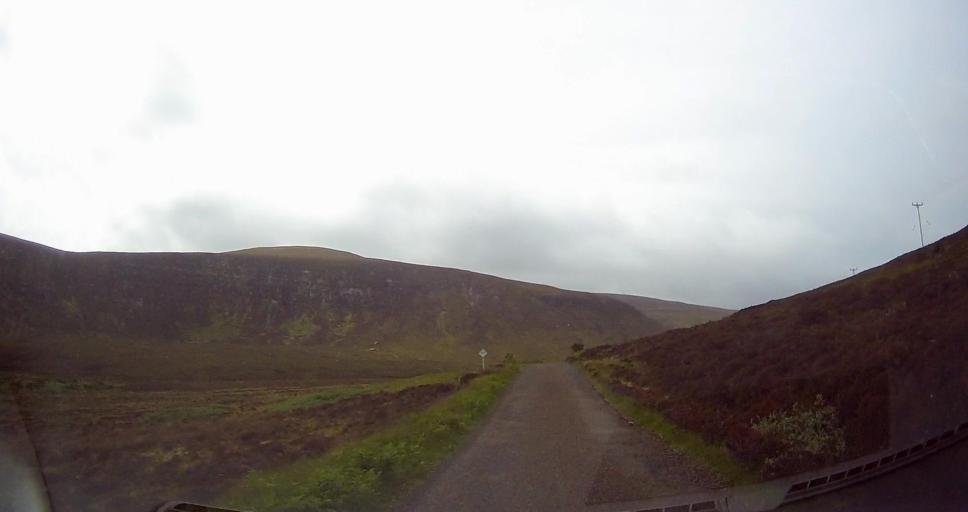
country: GB
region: Scotland
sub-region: Orkney Islands
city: Stromness
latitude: 58.8909
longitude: -3.3149
